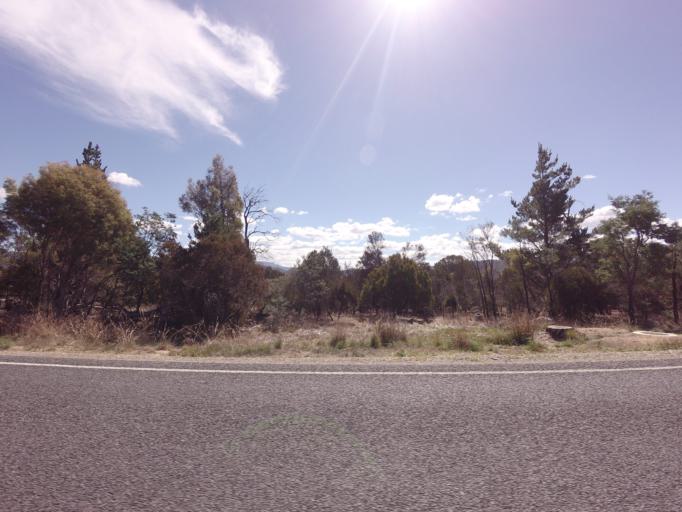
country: AU
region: Tasmania
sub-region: Break O'Day
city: St Helens
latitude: -41.6825
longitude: 147.8868
